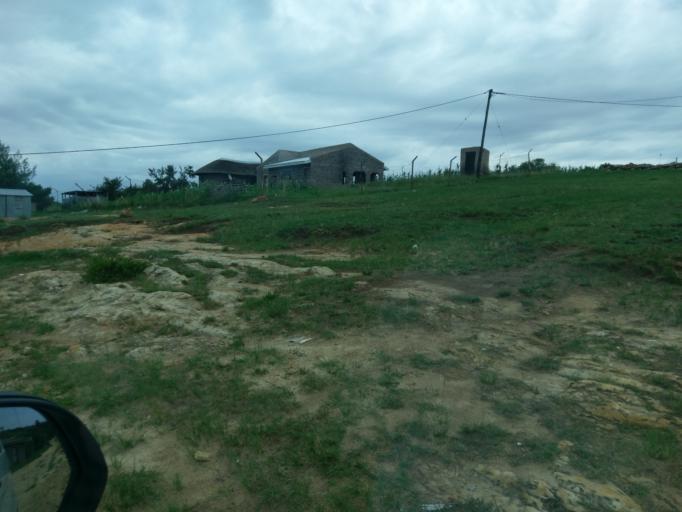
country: LS
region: Berea
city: Teyateyaneng
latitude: -29.1193
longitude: 27.9642
